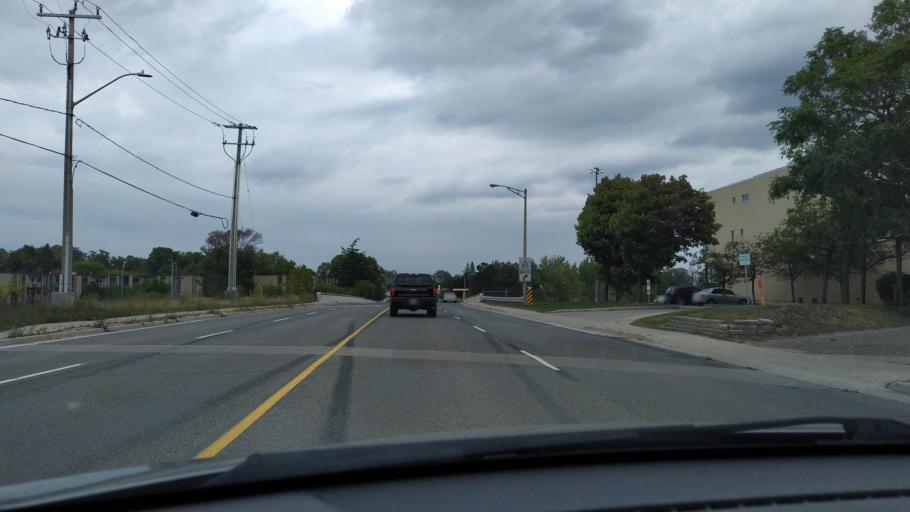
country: CA
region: Ontario
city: Waterloo
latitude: 43.4727
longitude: -80.4844
